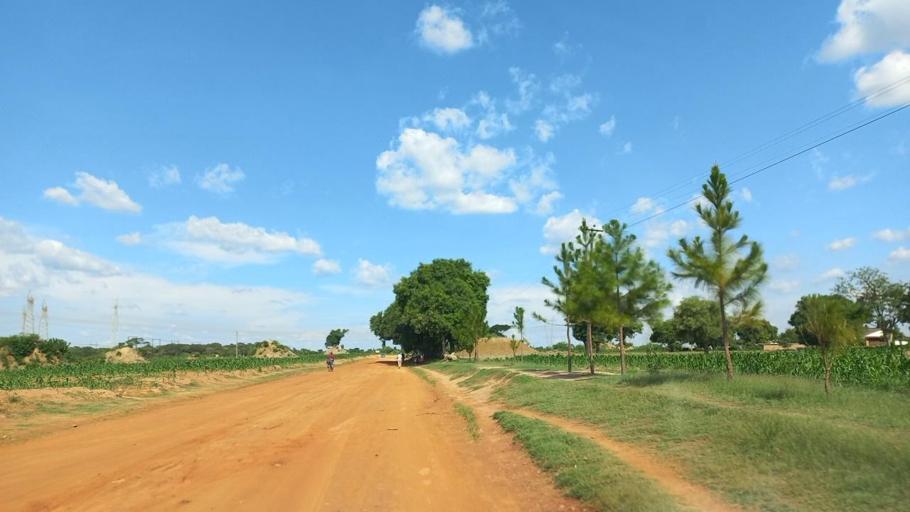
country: ZM
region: Copperbelt
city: Kitwe
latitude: -12.8715
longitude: 28.3412
